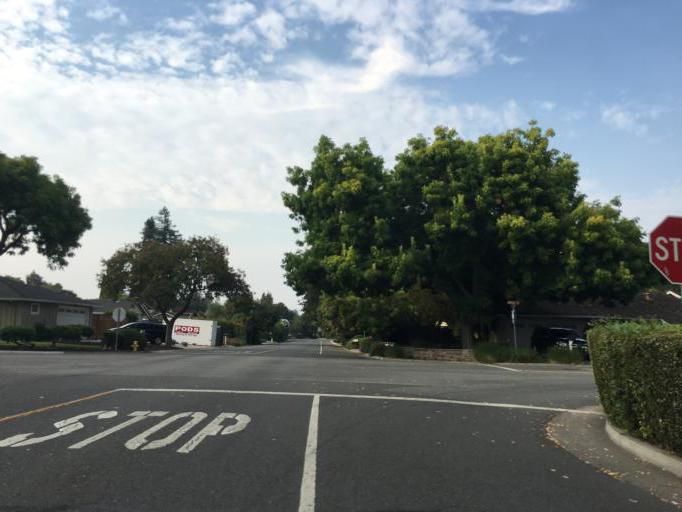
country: US
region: California
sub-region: Santa Clara County
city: Loyola
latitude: 37.3446
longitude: -122.0713
